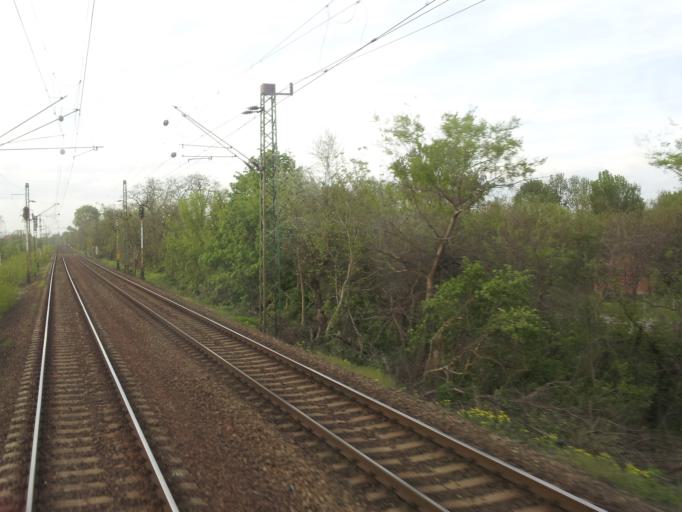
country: HU
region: Budapest
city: Budapest X. keruelet
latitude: 47.4975
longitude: 19.1588
